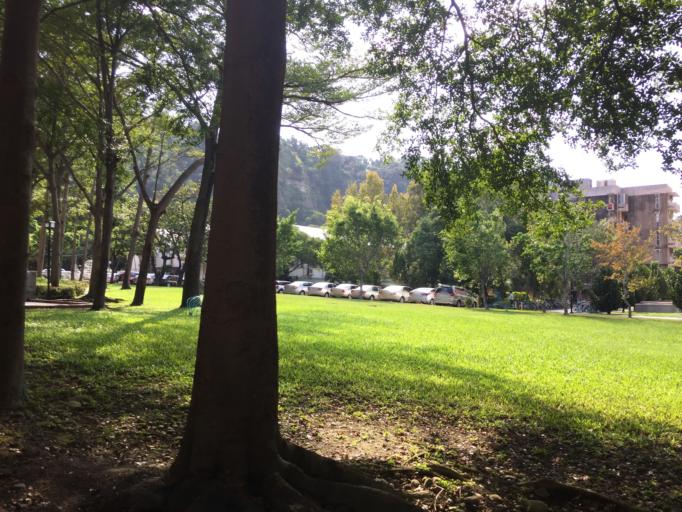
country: TW
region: Taiwan
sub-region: Changhua
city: Chang-hua
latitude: 24.0812
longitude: 120.5577
